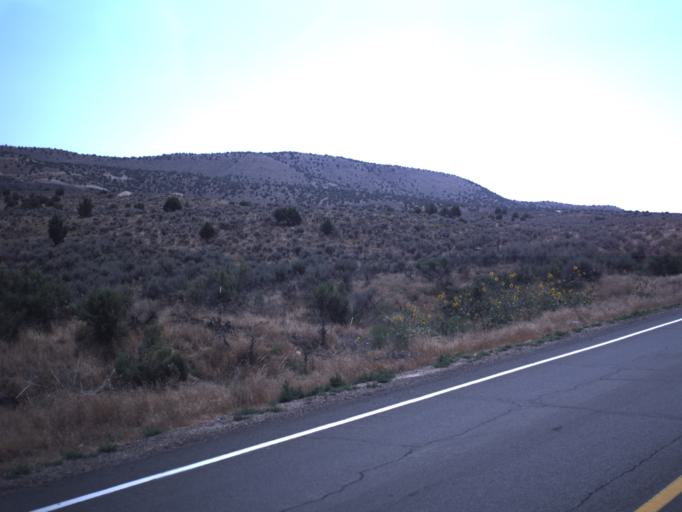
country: US
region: Utah
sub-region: Uintah County
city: Maeser
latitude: 40.4548
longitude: -109.6195
